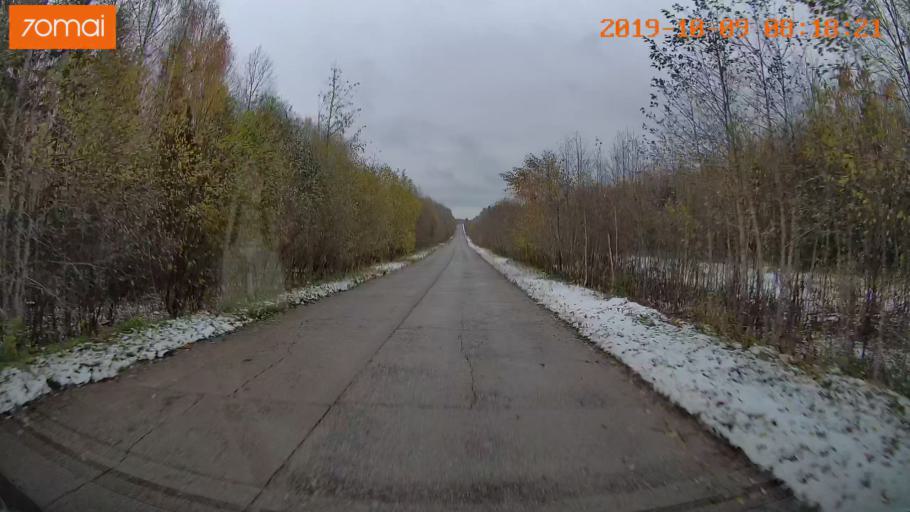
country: RU
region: Vologda
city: Gryazovets
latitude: 58.7402
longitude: 40.2221
